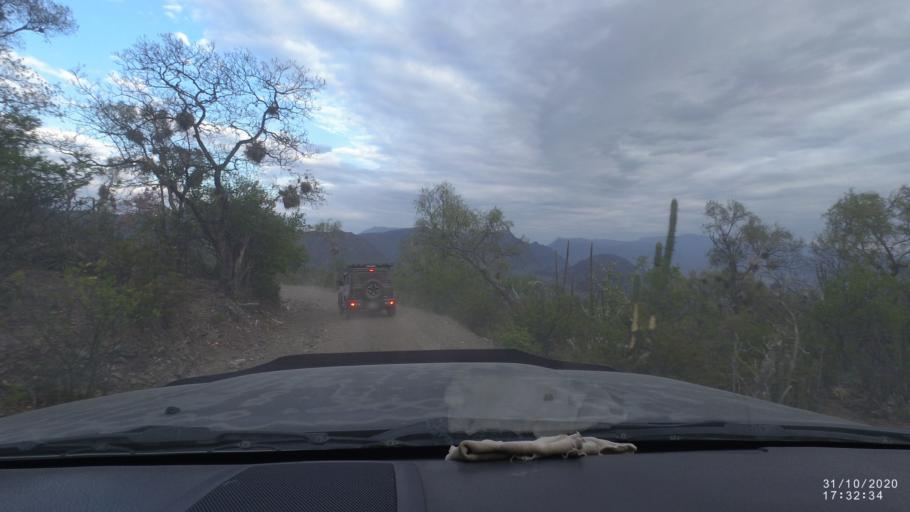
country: BO
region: Chuquisaca
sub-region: Provincia Zudanez
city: Mojocoya
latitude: -18.5995
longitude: -64.5529
